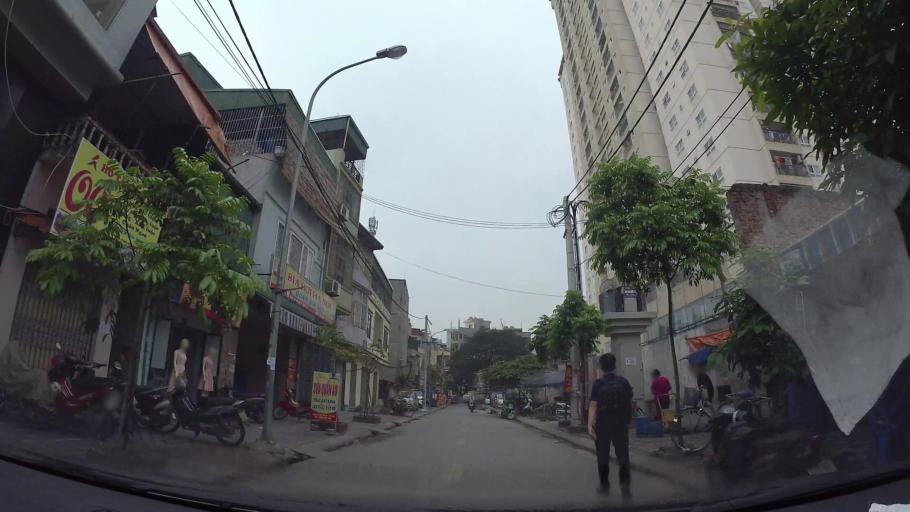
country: VN
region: Ha Noi
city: Hai BaTrung
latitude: 20.9933
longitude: 105.8579
